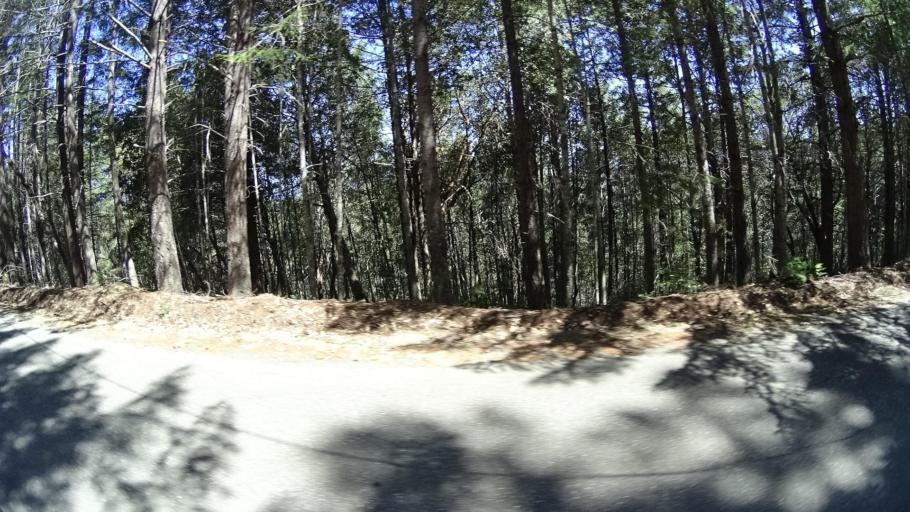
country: US
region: California
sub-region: Humboldt County
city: Redway
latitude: 40.1562
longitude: -124.0505
